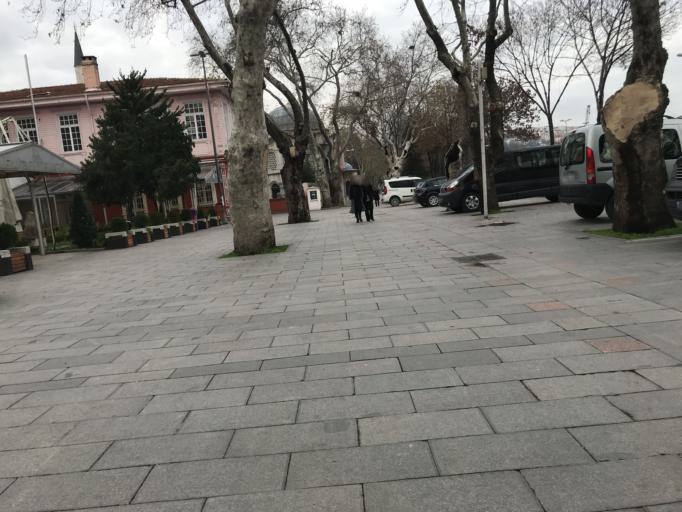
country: TR
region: Istanbul
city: Istanbul
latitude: 41.0436
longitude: 28.9368
